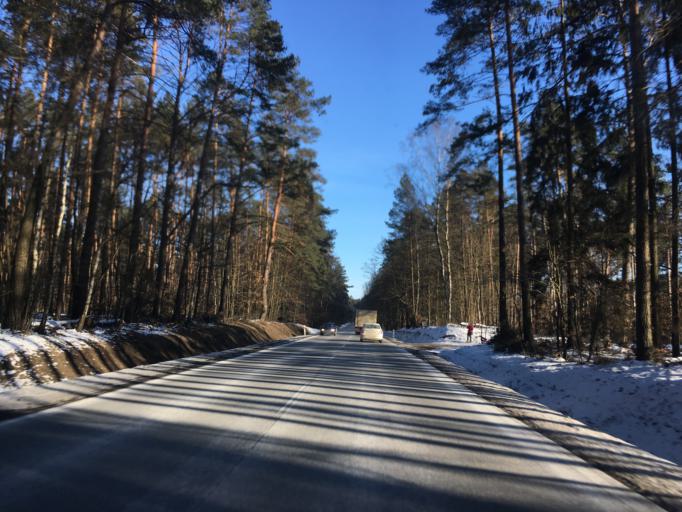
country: PL
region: Pomeranian Voivodeship
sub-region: Powiat koscierski
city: Koscierzyna
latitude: 54.1129
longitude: 17.9109
